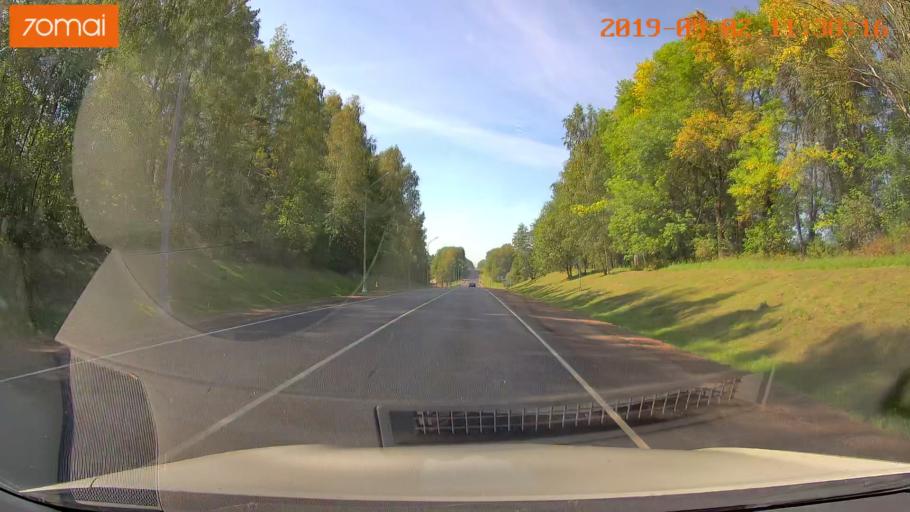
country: RU
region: Smolensk
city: Oster
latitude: 53.9142
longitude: 32.7436
